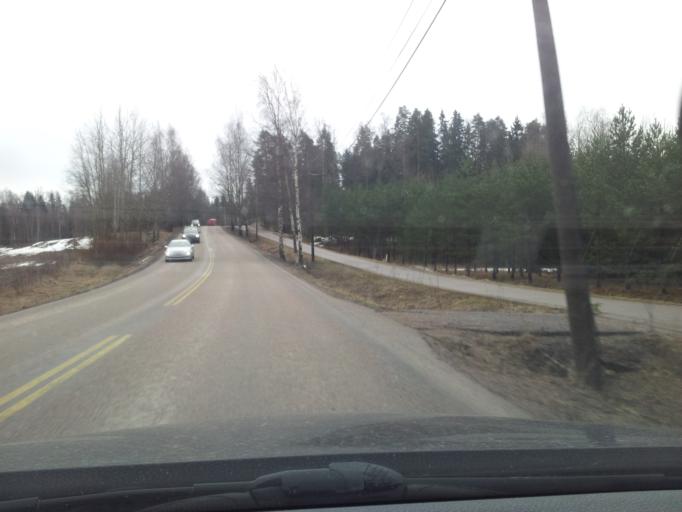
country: FI
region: Uusimaa
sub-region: Helsinki
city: Espoo
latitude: 60.1875
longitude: 24.6674
